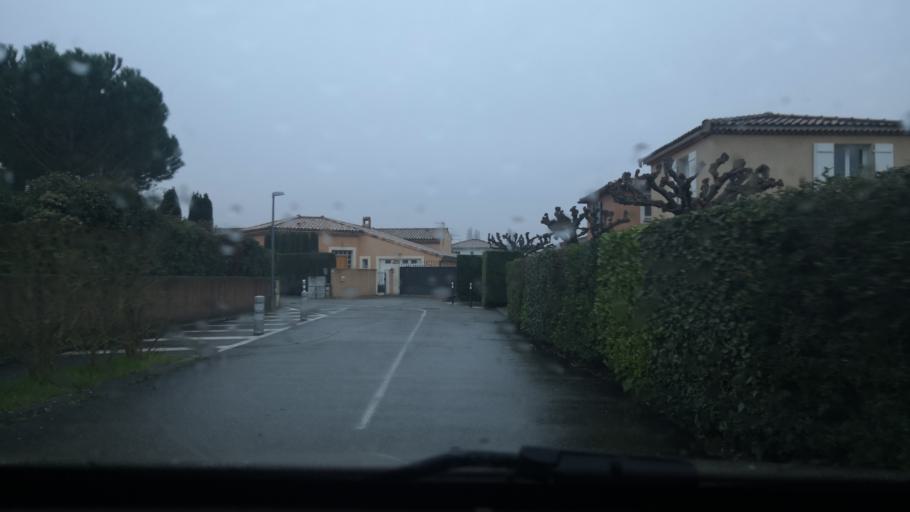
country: FR
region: Rhone-Alpes
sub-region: Departement de la Drome
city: Montboucher-sur-Jabron
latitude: 44.5435
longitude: 4.8022
